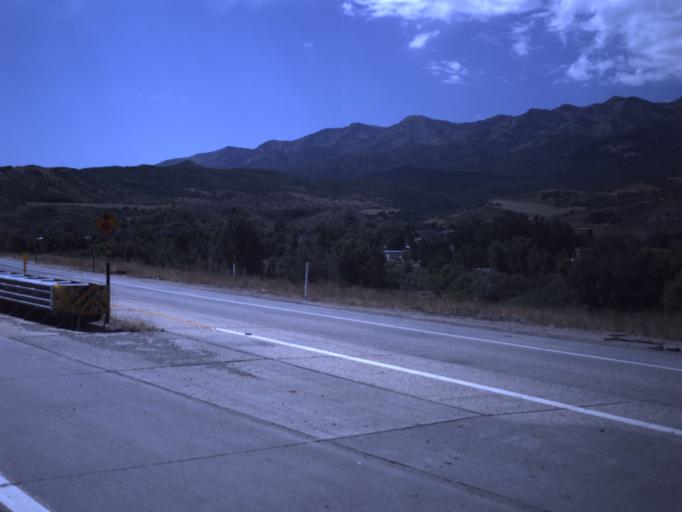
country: US
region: Utah
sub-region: Morgan County
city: Mountain Green
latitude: 41.1181
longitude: -111.7644
